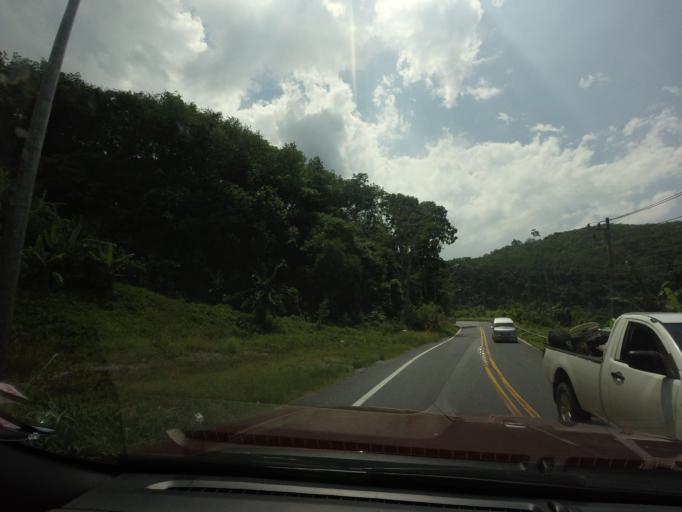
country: TH
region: Yala
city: Than To
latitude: 6.0328
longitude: 101.2085
